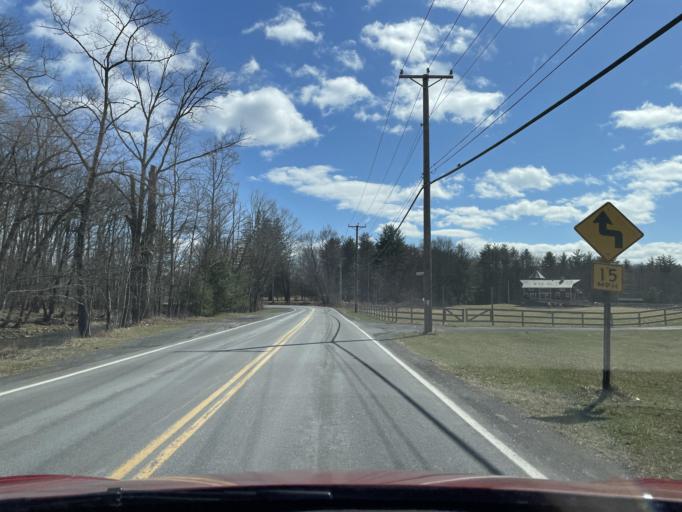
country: US
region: New York
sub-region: Ulster County
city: Zena
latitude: 42.0354
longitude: -74.0858
